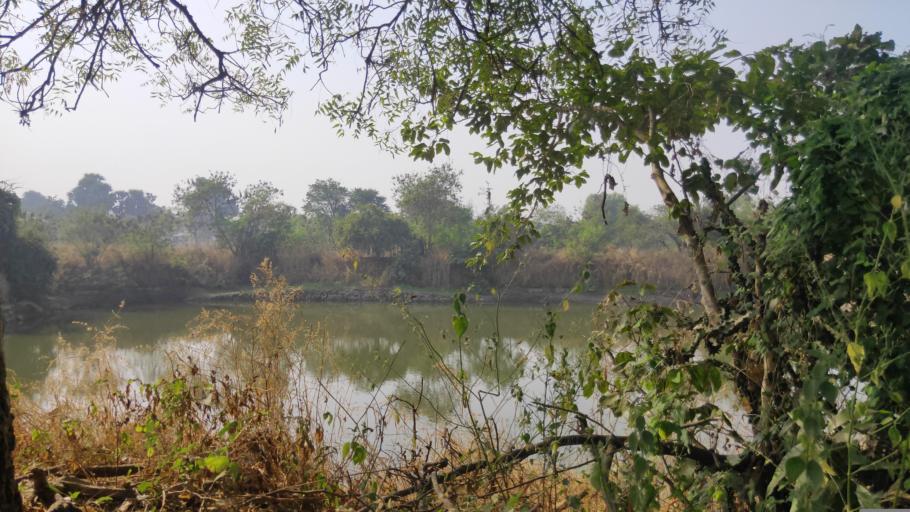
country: IN
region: Maharashtra
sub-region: Thane
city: Bhiwandi
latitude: 19.3103
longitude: 73.0901
